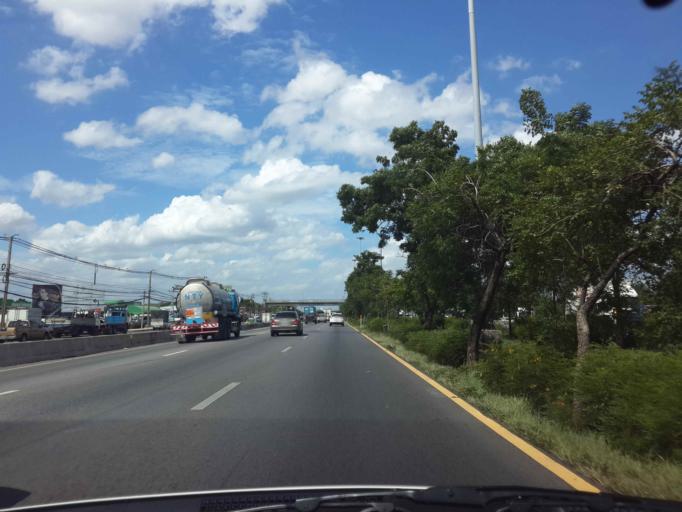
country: TH
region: Bangkok
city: Bang Bon
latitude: 13.6179
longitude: 100.3852
